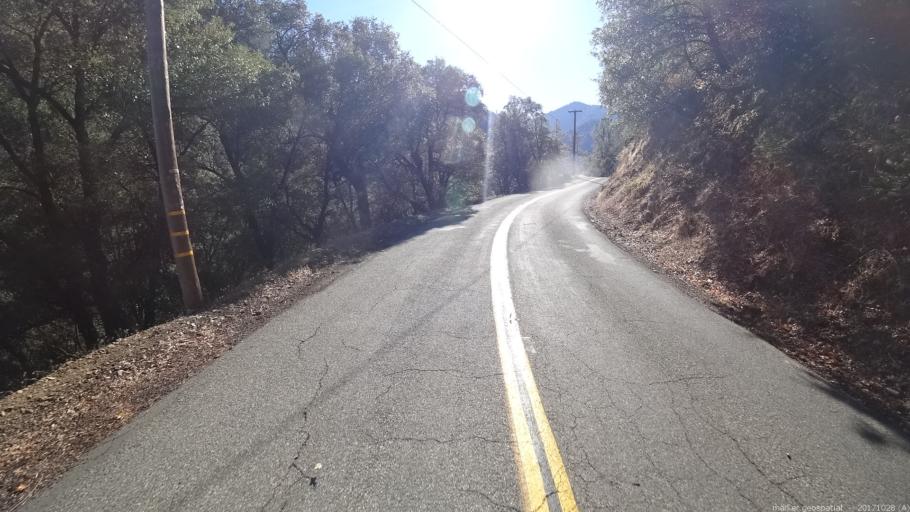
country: US
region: California
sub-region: Trinity County
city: Lewiston
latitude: 40.7731
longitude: -122.6115
